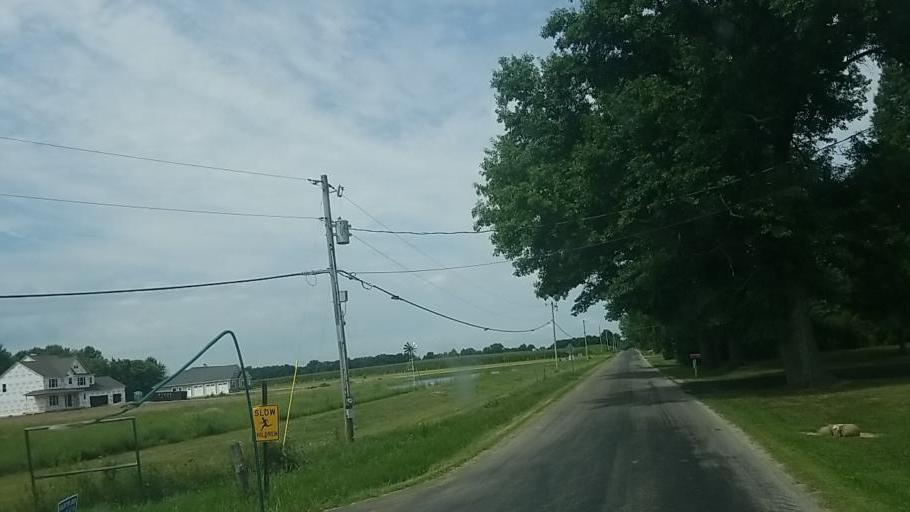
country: US
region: Ohio
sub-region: Delaware County
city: Sunbury
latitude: 40.2018
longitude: -82.7769
